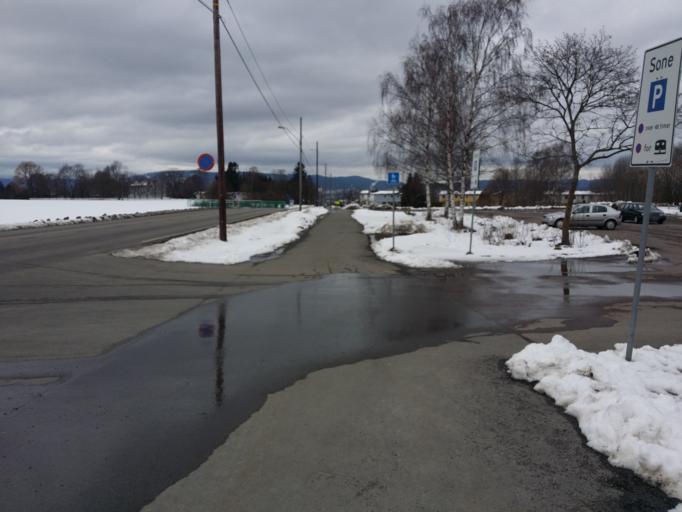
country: NO
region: Oslo
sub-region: Oslo
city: Oslo
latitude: 59.8959
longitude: 10.7772
